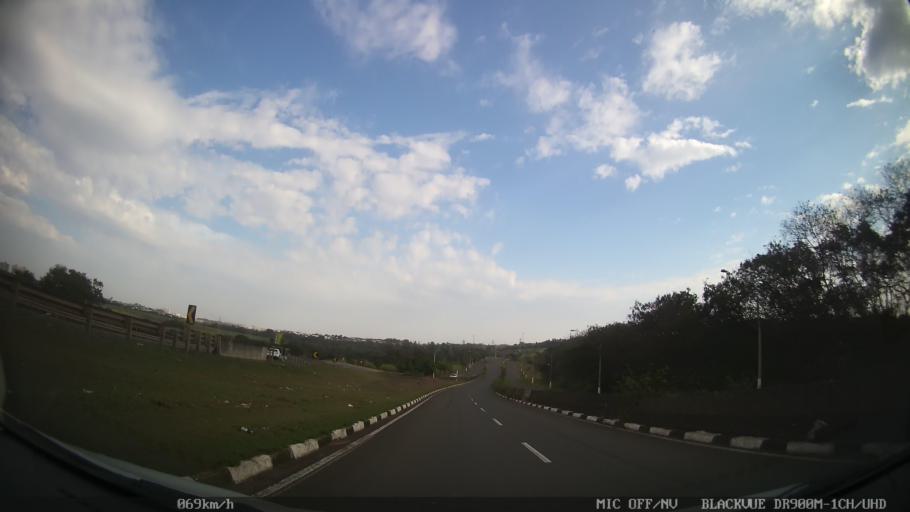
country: BR
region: Sao Paulo
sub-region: Paulinia
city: Paulinia
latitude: -22.7419
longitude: -47.1606
